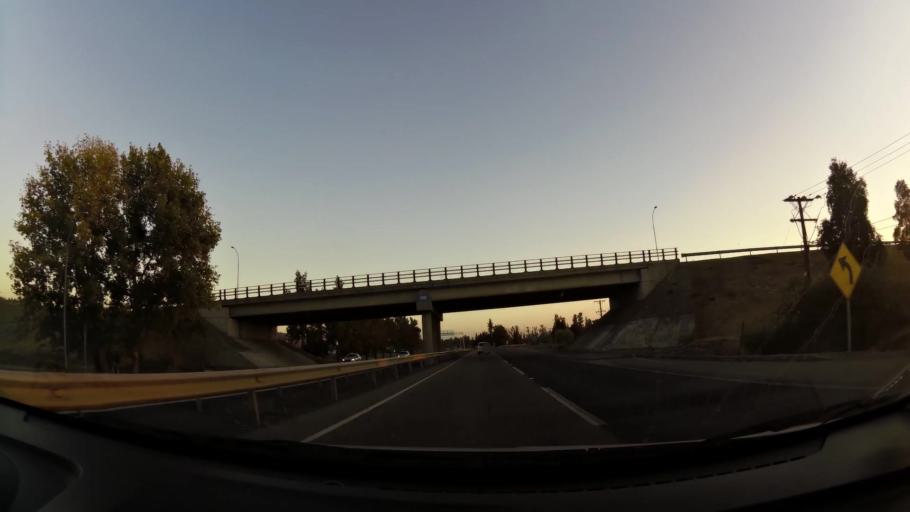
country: CL
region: Maule
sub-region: Provincia de Linares
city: Linares
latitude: -35.7601
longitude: -71.6714
